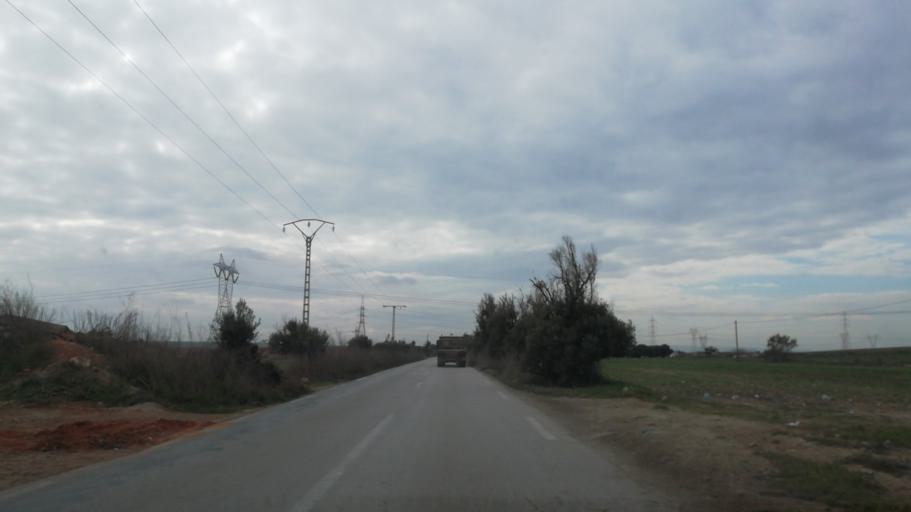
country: DZ
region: Oran
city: Ain el Bya
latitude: 35.7754
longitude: -0.3461
